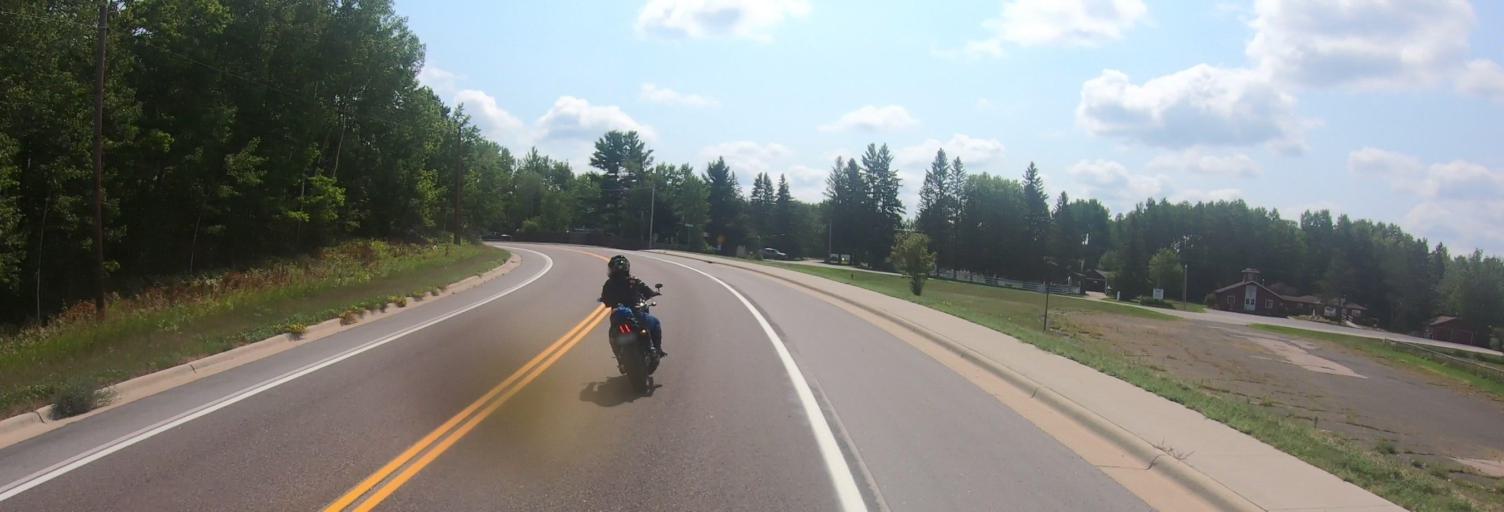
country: US
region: Minnesota
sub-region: Saint Louis County
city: Mountain Iron
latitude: 48.0509
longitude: -92.8289
